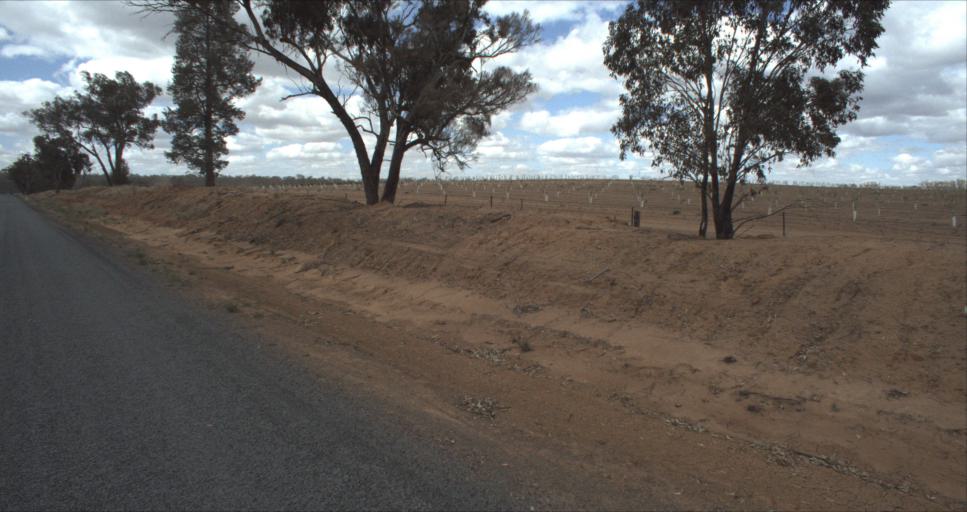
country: AU
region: New South Wales
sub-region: Leeton
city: Leeton
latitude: -34.6499
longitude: 146.3514
